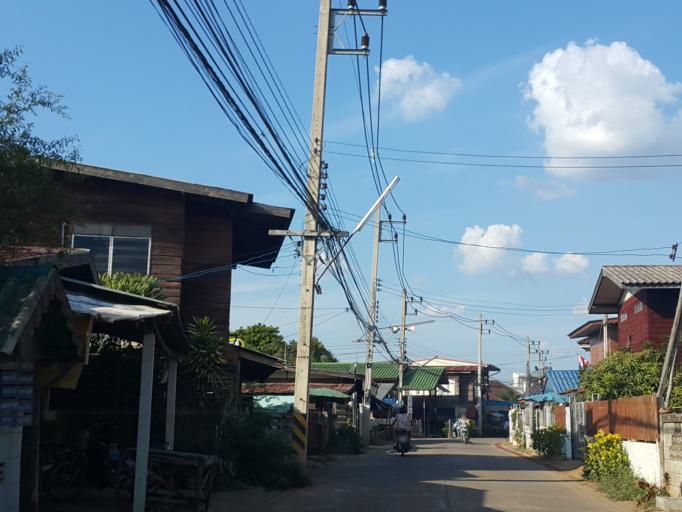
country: TH
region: Sukhothai
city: Thung Saliam
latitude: 17.3148
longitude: 99.5530
